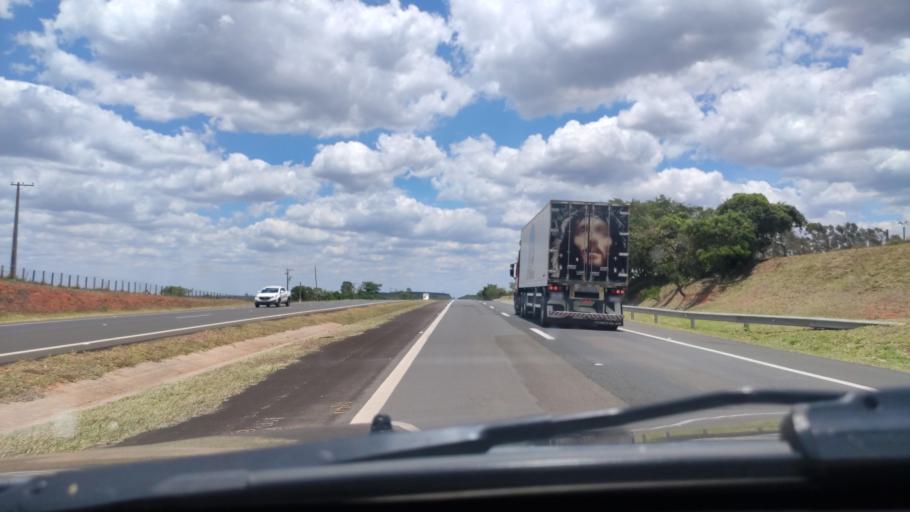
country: BR
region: Sao Paulo
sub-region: Duartina
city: Duartina
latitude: -22.5011
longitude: -49.2765
